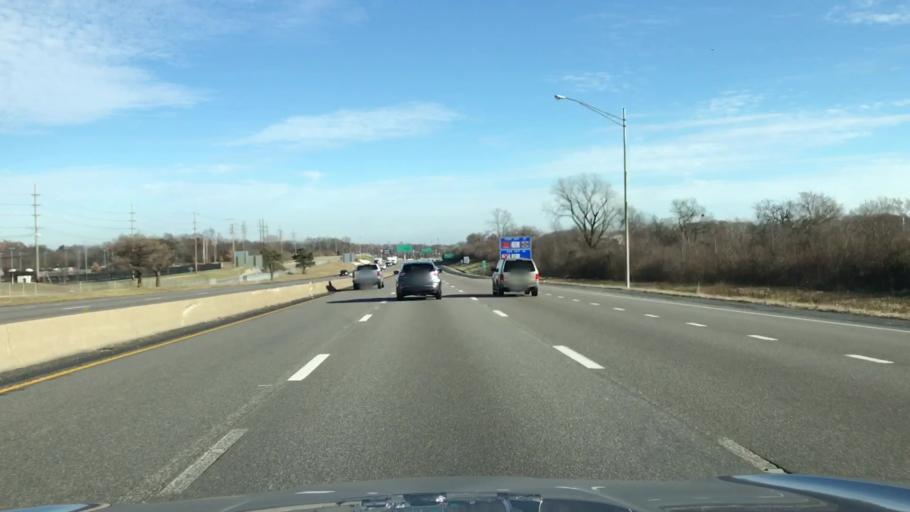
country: US
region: Missouri
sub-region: Saint Louis County
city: Castle Point
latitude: 38.7706
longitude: -90.2337
